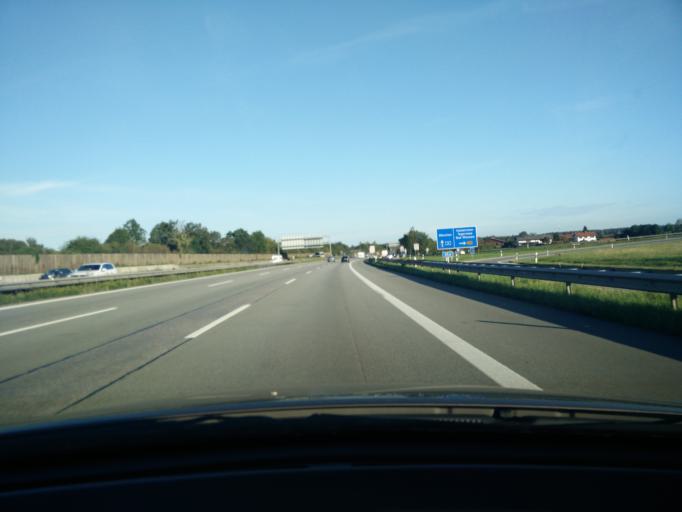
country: DE
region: Bavaria
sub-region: Upper Bavaria
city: Holzkirchen
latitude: 47.8948
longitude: 11.7256
